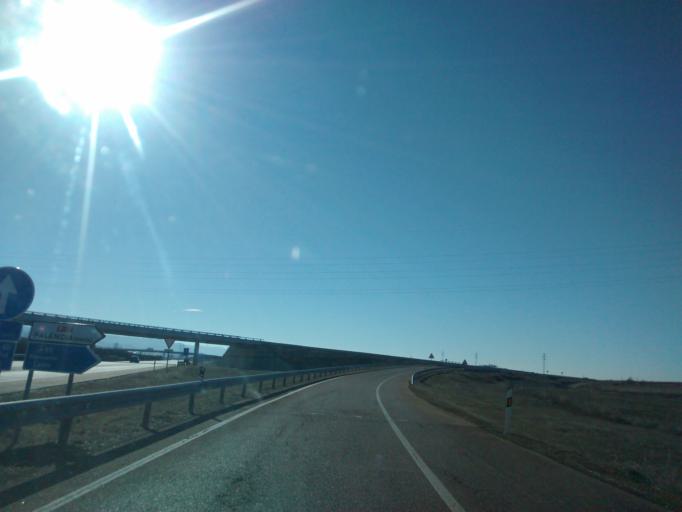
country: ES
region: Castille and Leon
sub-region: Provincia de Palencia
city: Fuentes de Valdepero
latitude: 42.0622
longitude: -4.4931
